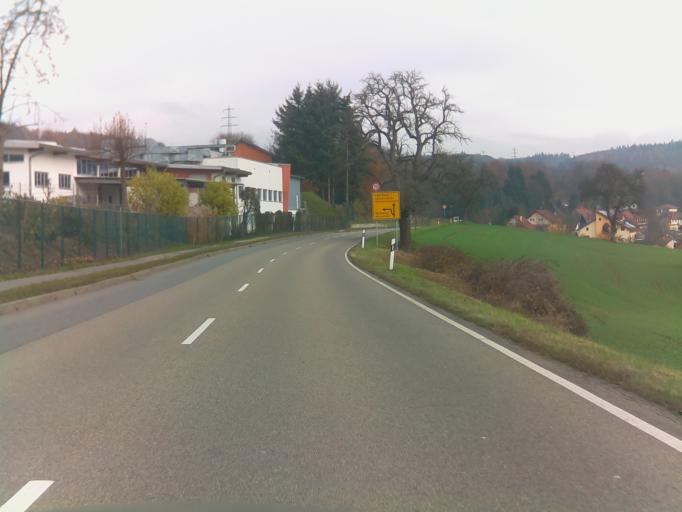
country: DE
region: Baden-Wuerttemberg
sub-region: Karlsruhe Region
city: Spechbach
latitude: 49.3721
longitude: 8.8802
